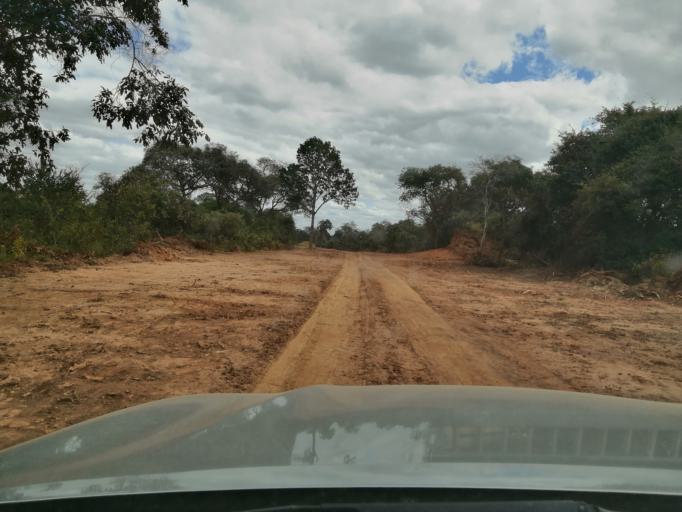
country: ZM
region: Central
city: Mumbwa
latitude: -14.5856
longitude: 27.2085
